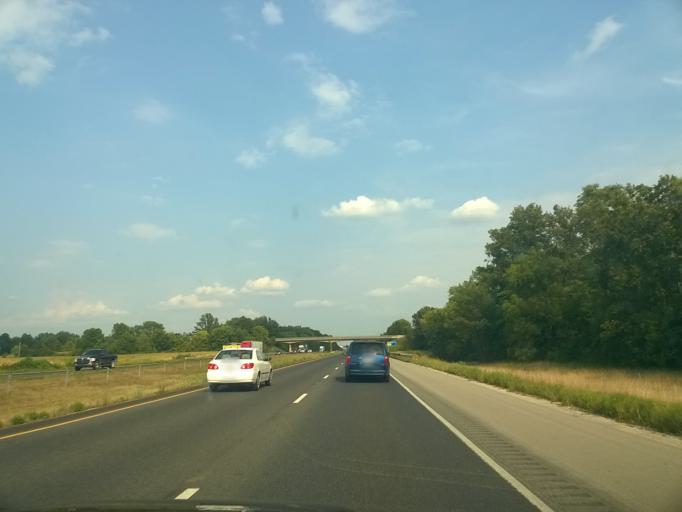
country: US
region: Indiana
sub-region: Vigo County
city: Terre Haute
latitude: 39.4307
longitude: -87.3601
